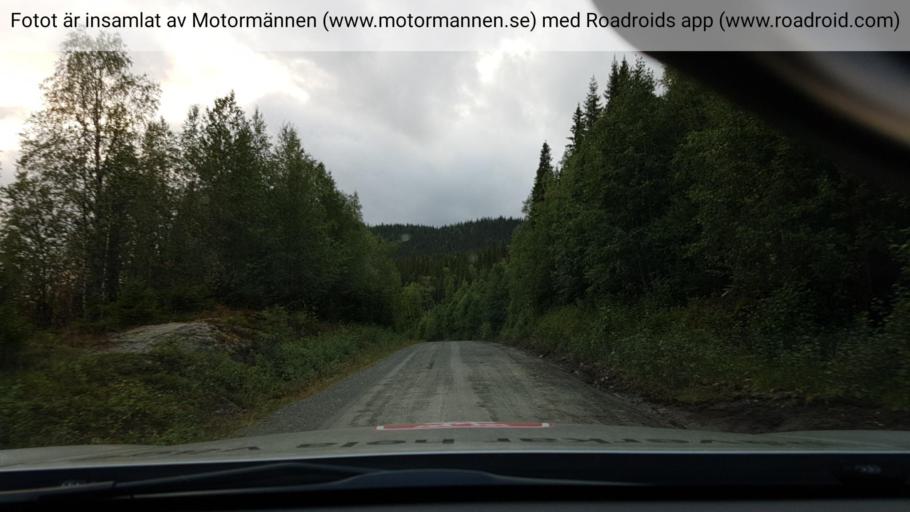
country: SE
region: Vaesterbotten
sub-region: Vilhelmina Kommun
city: Sjoberg
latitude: 65.4986
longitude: 15.5448
